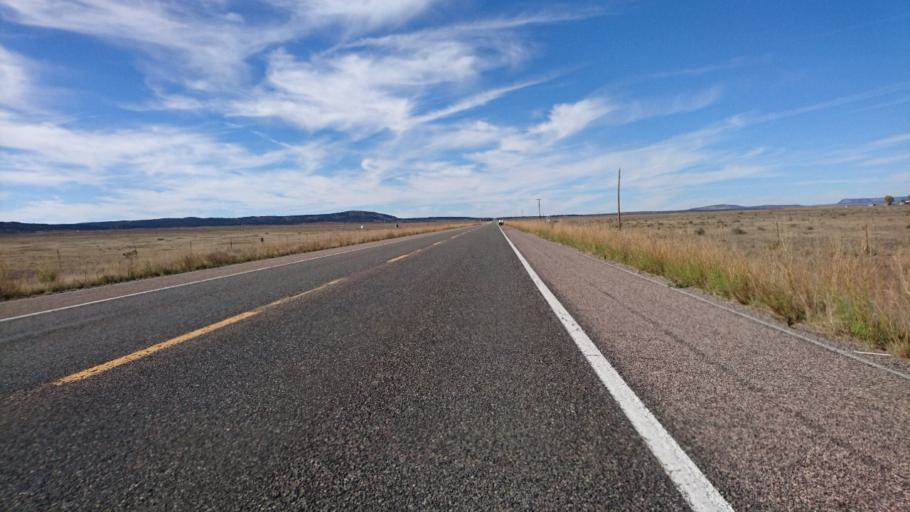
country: US
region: Arizona
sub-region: Mohave County
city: Peach Springs
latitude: 35.4637
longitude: -113.1147
